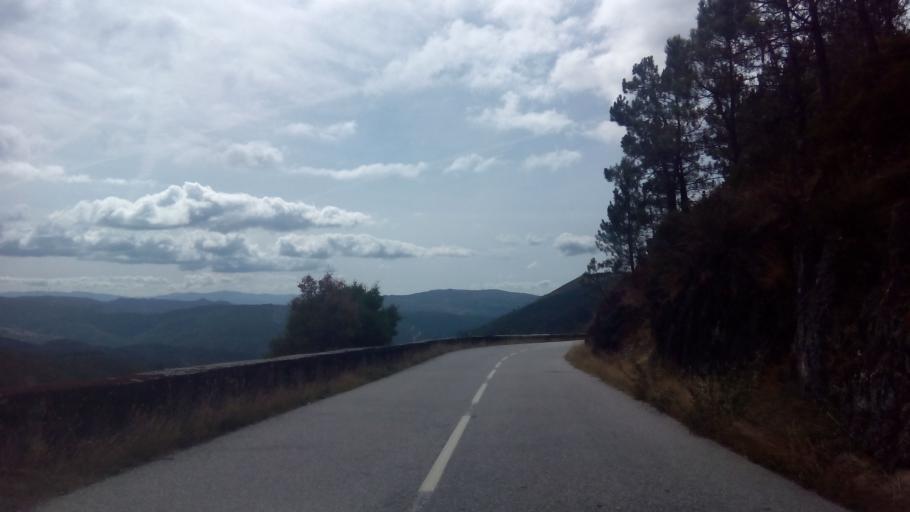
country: PT
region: Vila Real
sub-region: Mesao Frio
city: Mesao Frio
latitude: 41.2769
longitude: -7.9289
